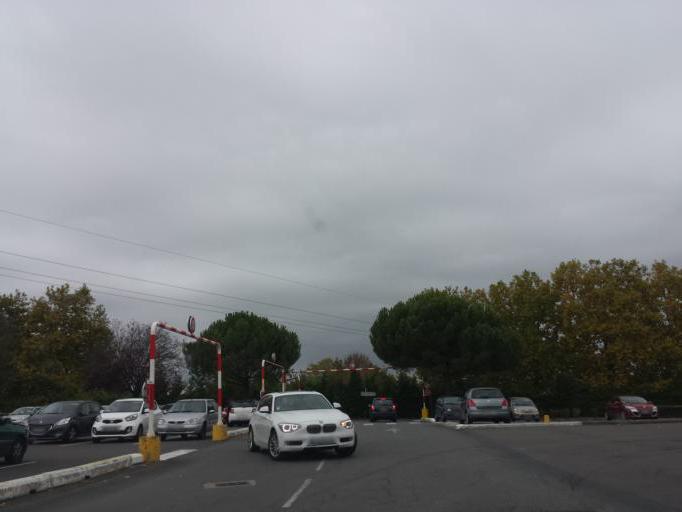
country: FR
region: Poitou-Charentes
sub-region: Departement de la Charente
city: La Couronne
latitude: 45.6199
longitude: 0.1054
